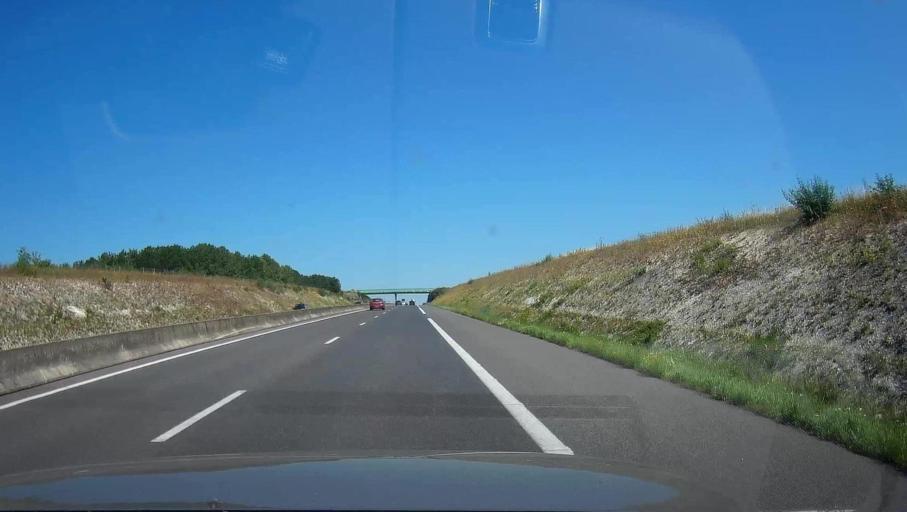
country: FR
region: Champagne-Ardenne
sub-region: Departement de l'Aube
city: Mailly-le-Camp
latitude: 48.7996
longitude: 4.2781
